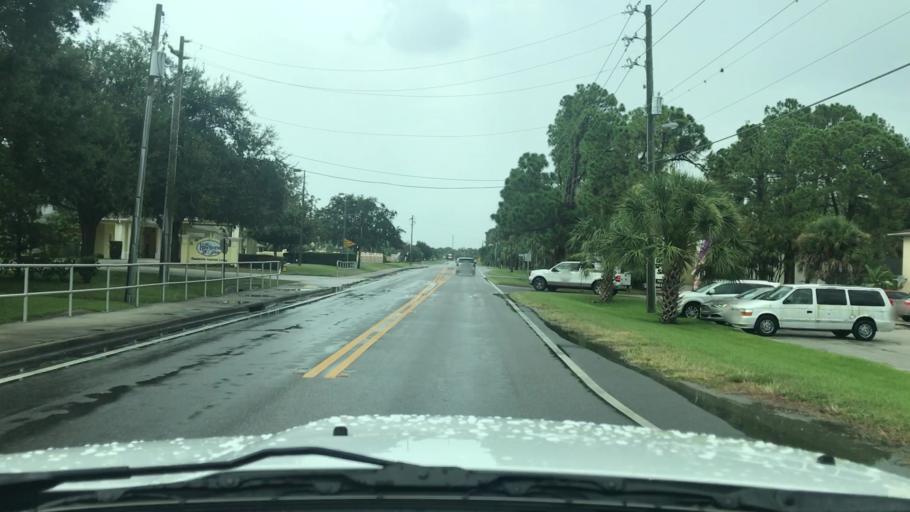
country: US
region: Florida
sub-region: Polk County
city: Cypress Gardens
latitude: 28.0099
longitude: -81.6806
